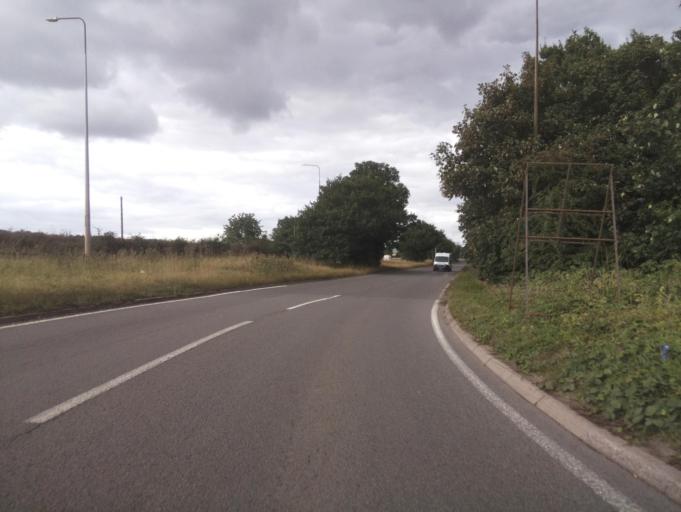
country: GB
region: England
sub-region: Solihull
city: Chelmsley Wood
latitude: 52.4781
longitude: -1.7072
